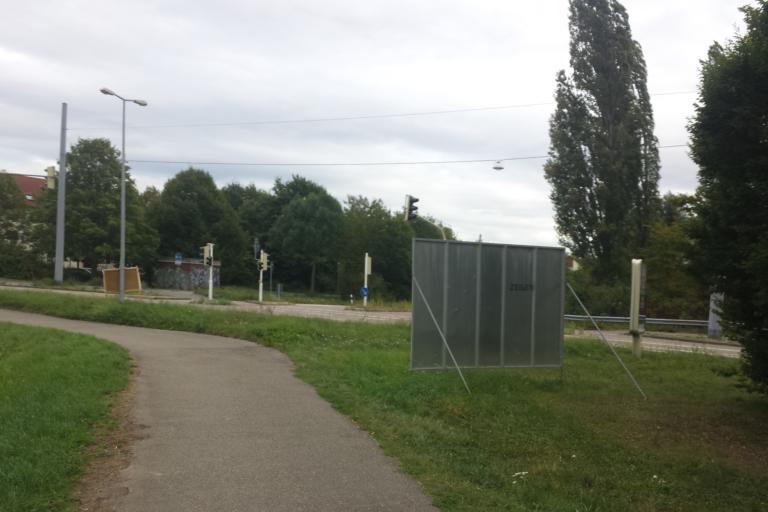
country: DE
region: Baden-Wuerttemberg
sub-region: Karlsruhe Region
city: Ilvesheim
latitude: 49.4989
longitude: 8.5368
